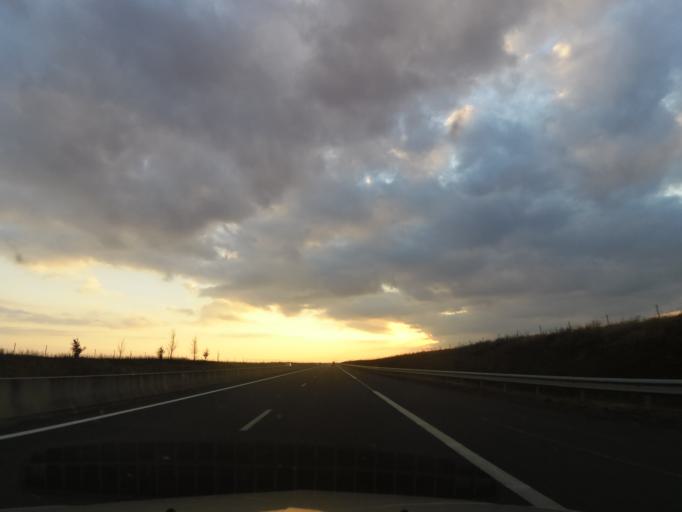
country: FR
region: Centre
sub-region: Departement du Loiret
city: Ascheres-le-Marche
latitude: 48.0679
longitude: 1.9604
